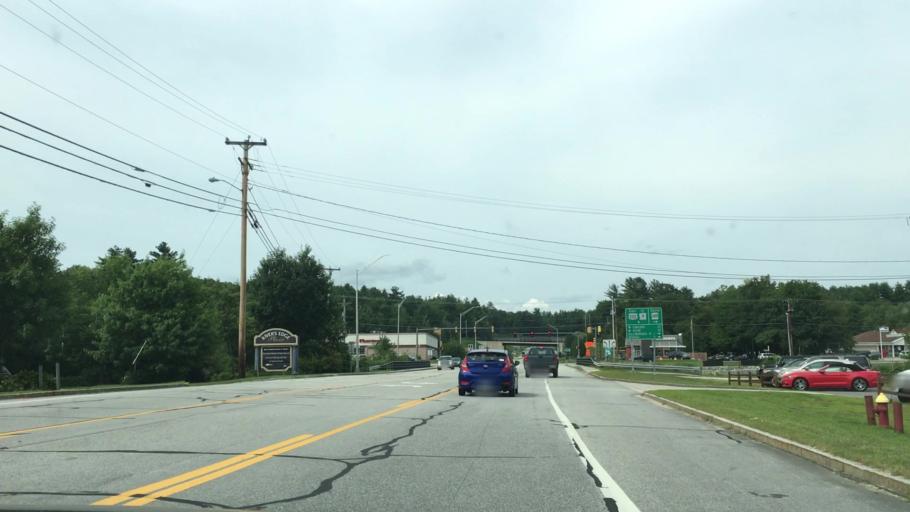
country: US
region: New Hampshire
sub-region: Hillsborough County
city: Hillsborough
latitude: 43.1104
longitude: -71.9195
